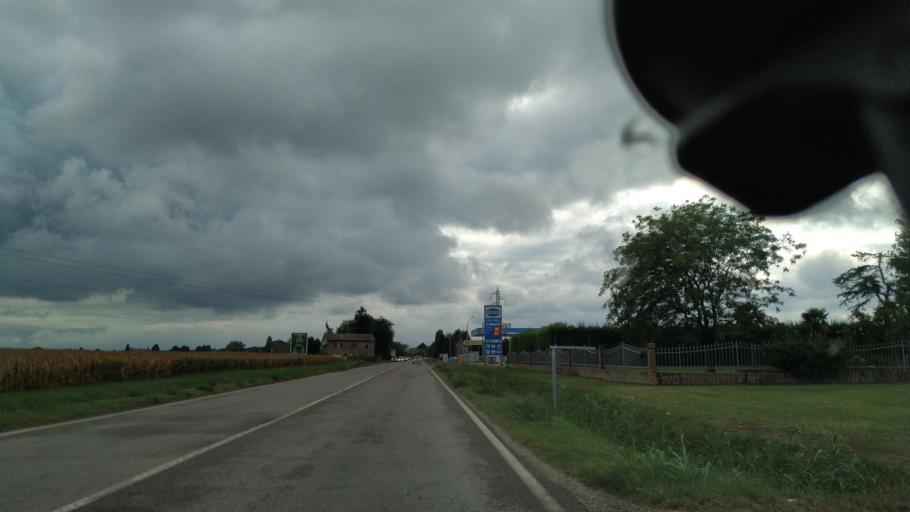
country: IT
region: Emilia-Romagna
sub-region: Provincia di Ferrara
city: Cento
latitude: 44.7466
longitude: 11.2913
